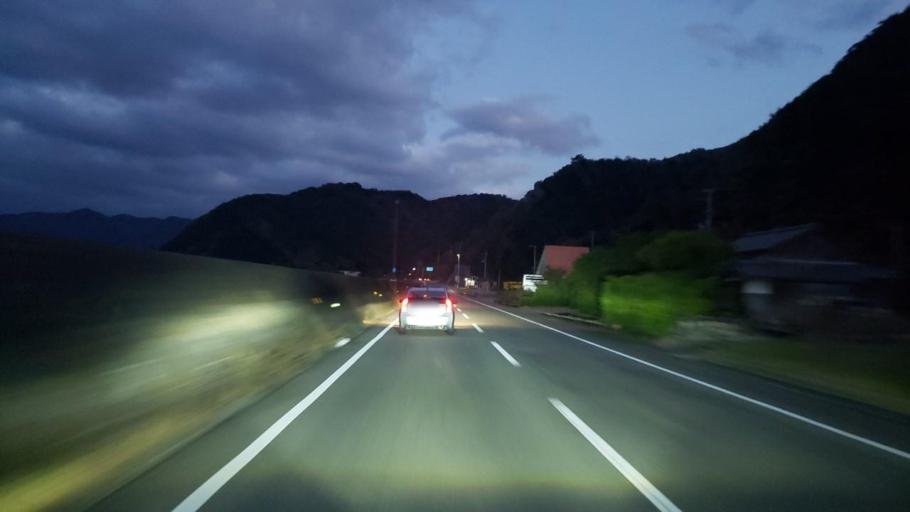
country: JP
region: Tokushima
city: Ishii
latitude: 34.2065
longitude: 134.4458
